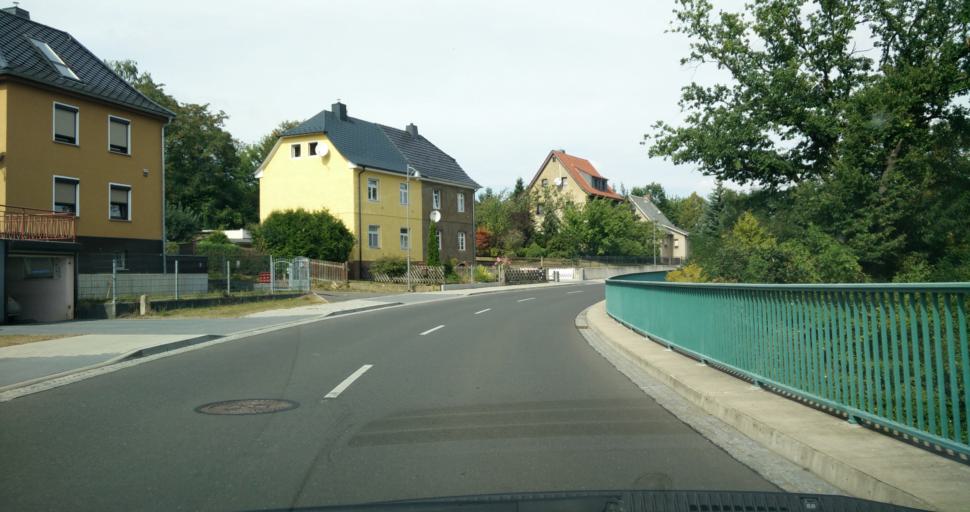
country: DE
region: Saxony
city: Colditz
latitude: 51.1266
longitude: 12.7980
